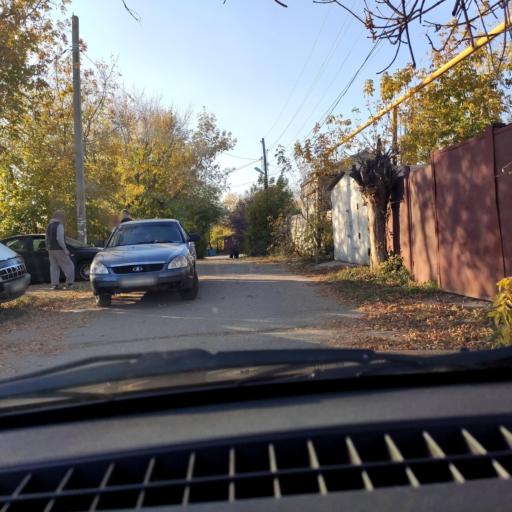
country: RU
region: Bashkortostan
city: Ufa
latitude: 54.7012
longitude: 55.9837
